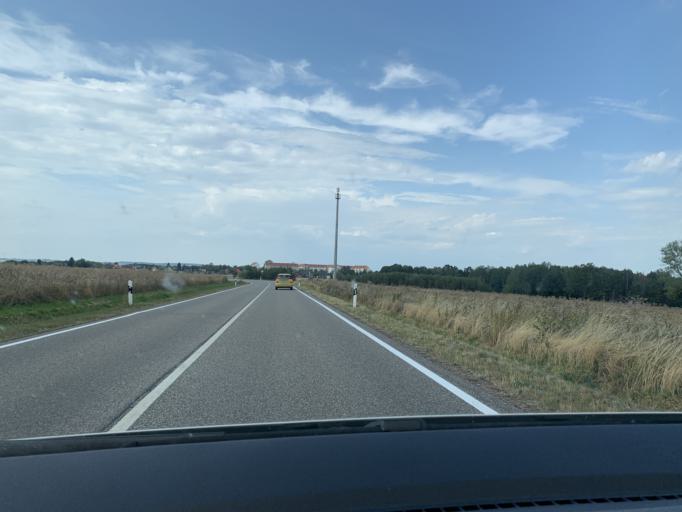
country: DE
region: Saxony
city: Frankenberg
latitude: 50.9093
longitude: 13.0693
